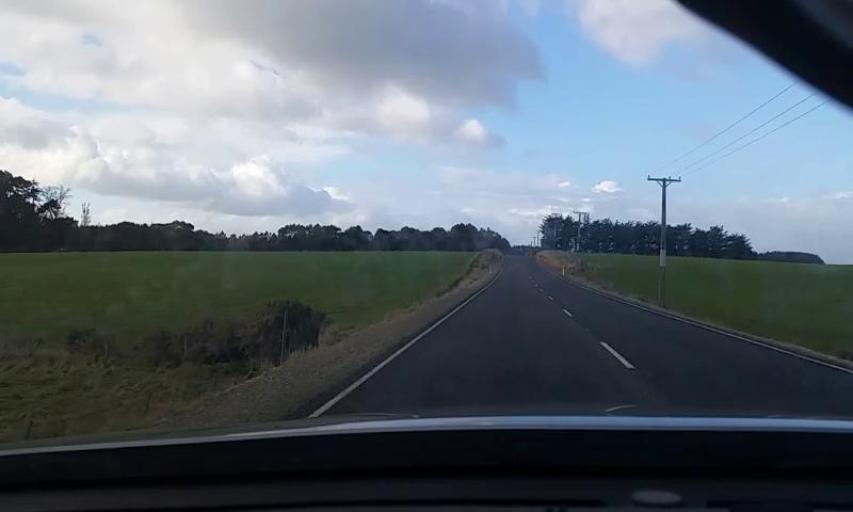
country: NZ
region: Southland
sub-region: Invercargill City
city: Invercargill
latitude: -46.3807
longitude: 168.4244
